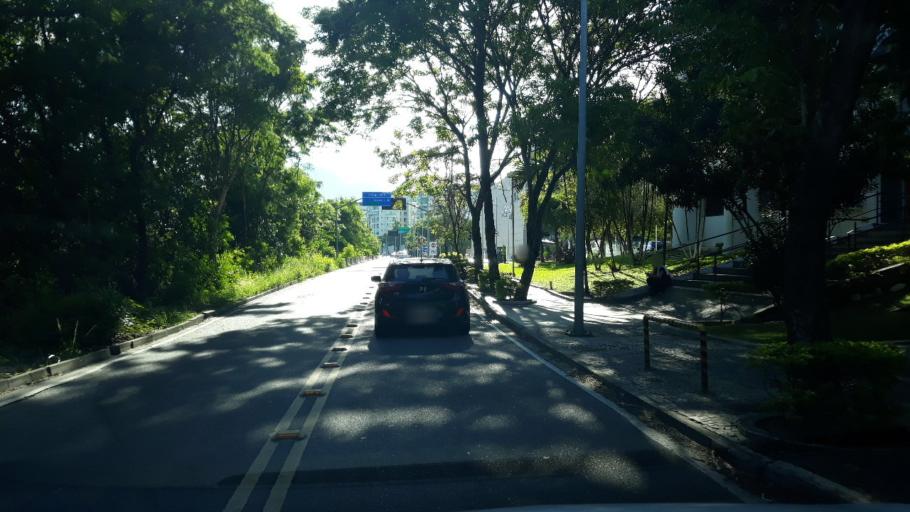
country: BR
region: Rio de Janeiro
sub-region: Rio De Janeiro
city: Rio de Janeiro
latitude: -22.9966
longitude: -43.3525
